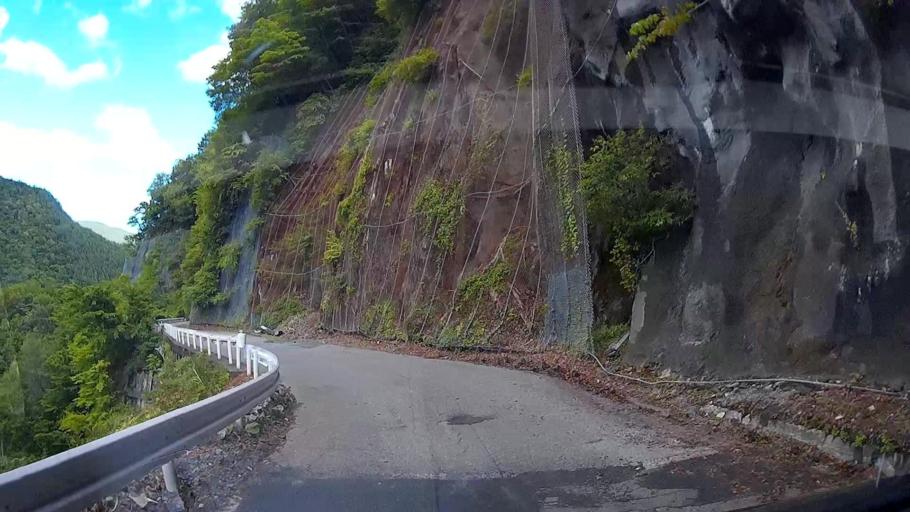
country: JP
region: Shizuoka
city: Shizuoka-shi
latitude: 35.3164
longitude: 138.1837
